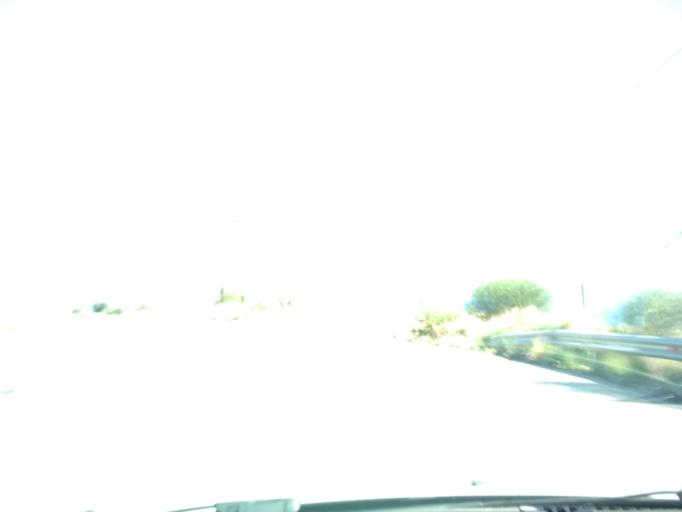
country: GR
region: Central Greece
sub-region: Nomos Evvoias
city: Oreoi
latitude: 38.8419
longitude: 23.0974
